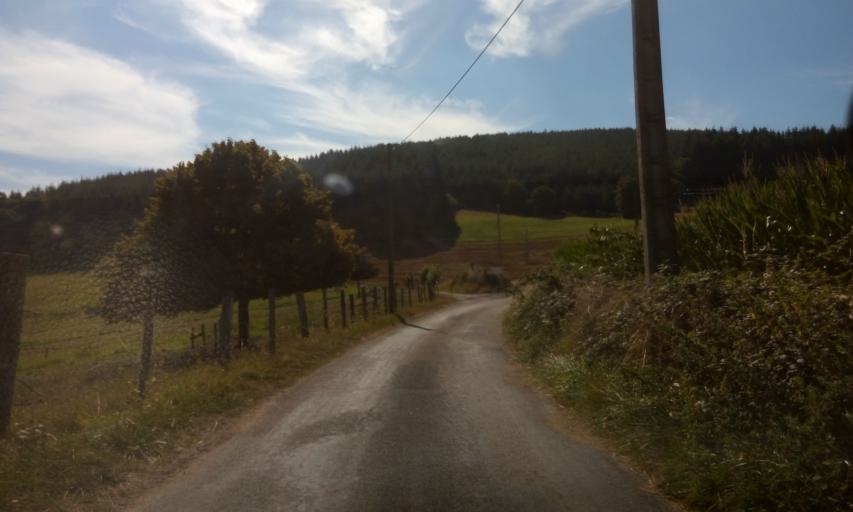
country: FR
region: Rhone-Alpes
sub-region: Departement du Rhone
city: Amplepuis
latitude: 45.9662
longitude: 4.3513
